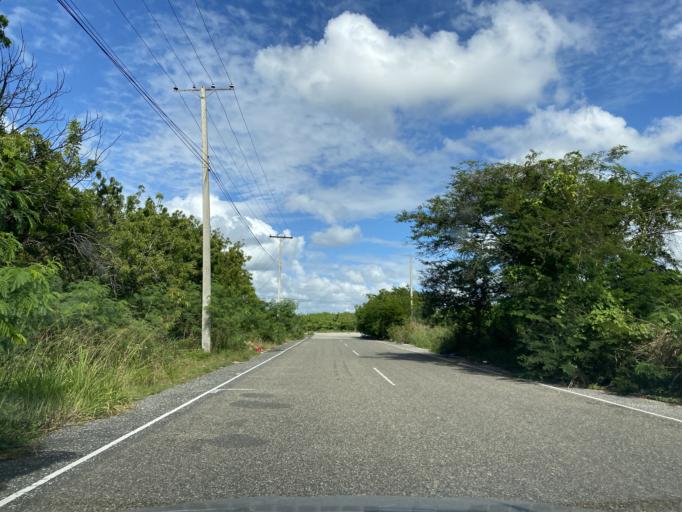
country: DO
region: Santo Domingo
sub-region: Santo Domingo
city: Boca Chica
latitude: 18.4508
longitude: -69.5939
